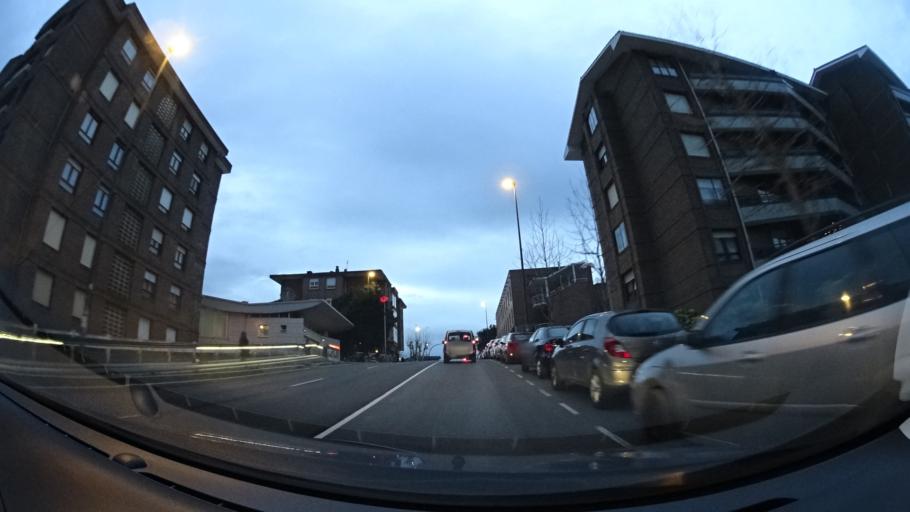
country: ES
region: Basque Country
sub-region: Bizkaia
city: Getxo
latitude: 43.3573
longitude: -3.0112
